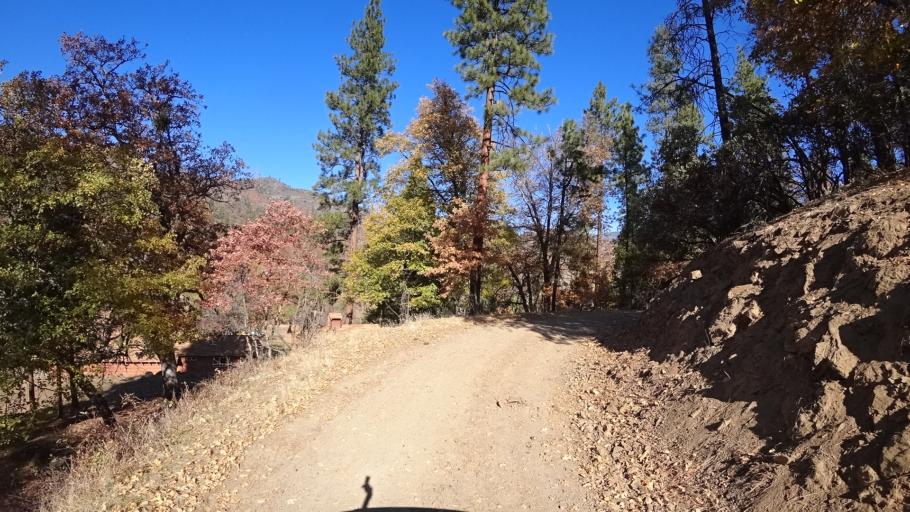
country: US
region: California
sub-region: Siskiyou County
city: Yreka
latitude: 41.8594
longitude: -122.8247
